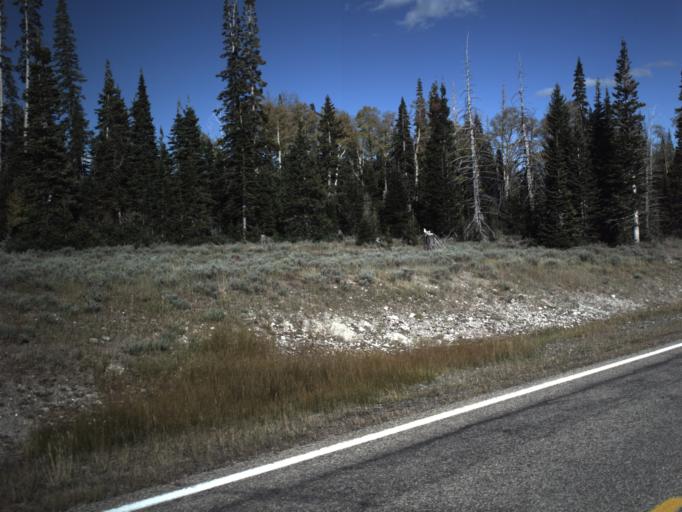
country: US
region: Utah
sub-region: Iron County
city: Parowan
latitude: 37.6507
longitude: -112.7920
